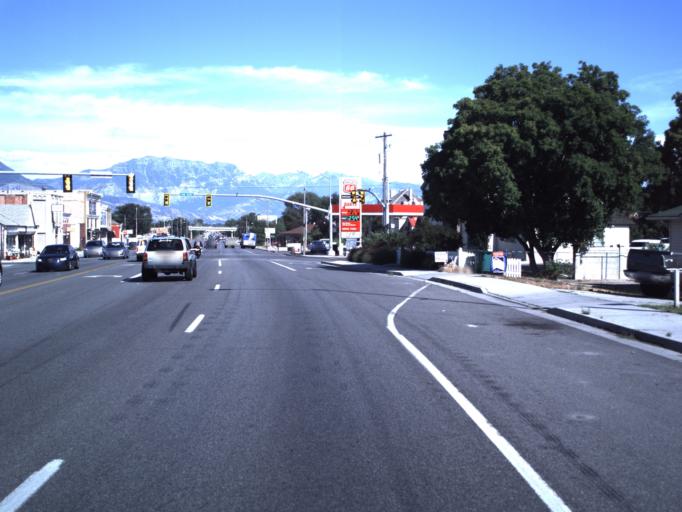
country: US
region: Utah
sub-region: Utah County
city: Lehi
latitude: 40.3974
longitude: -111.8487
